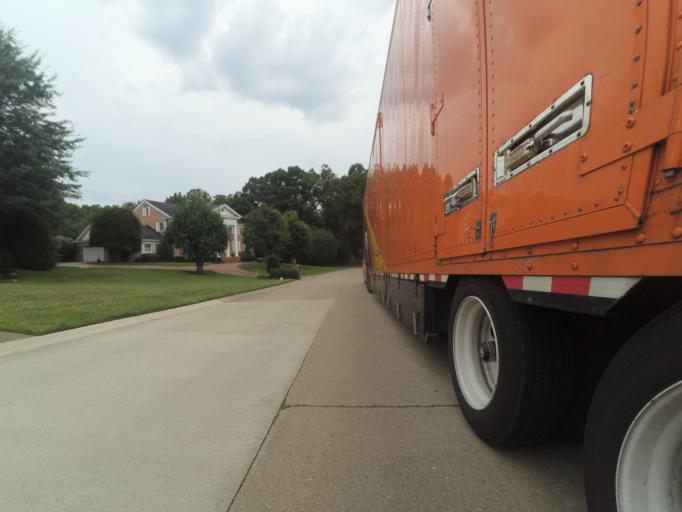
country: US
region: West Virginia
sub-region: Cabell County
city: Huntington
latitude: 38.4014
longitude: -82.3960
